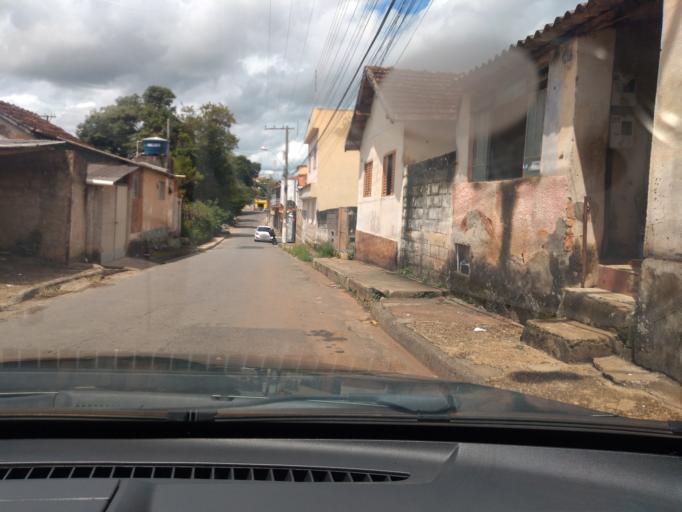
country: BR
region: Minas Gerais
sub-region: Tres Coracoes
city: Tres Coracoes
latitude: -21.6971
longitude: -45.2641
